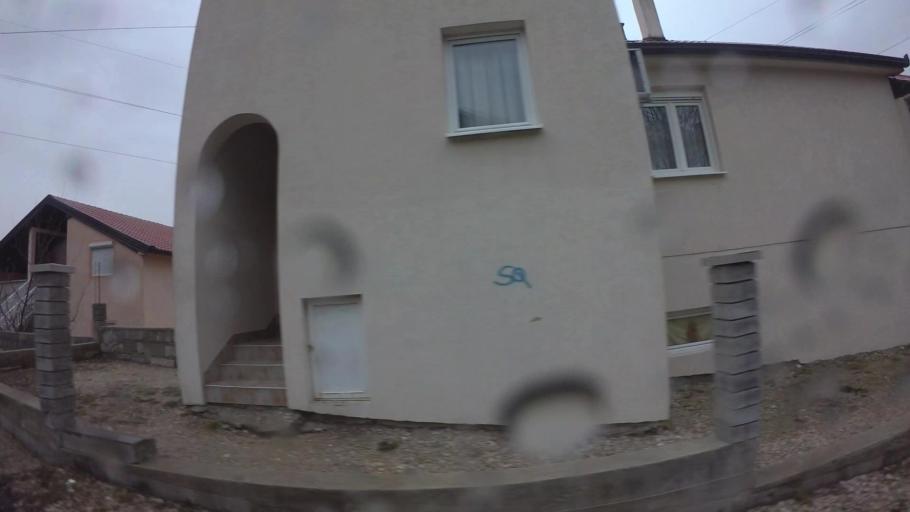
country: BA
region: Federation of Bosnia and Herzegovina
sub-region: Hercegovacko-Bosanski Kanton
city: Mostar
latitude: 43.3531
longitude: 17.8179
